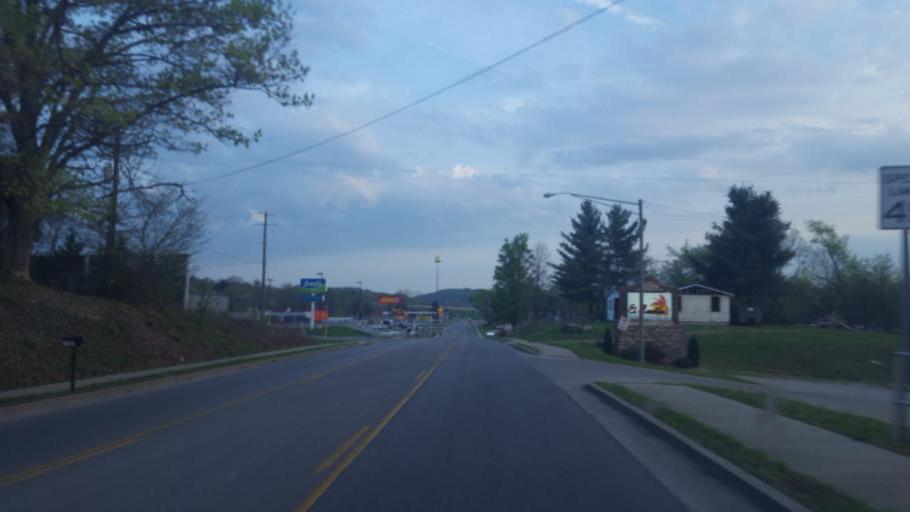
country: US
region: Kentucky
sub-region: Hart County
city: Munfordville
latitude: 37.2846
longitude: -85.8997
